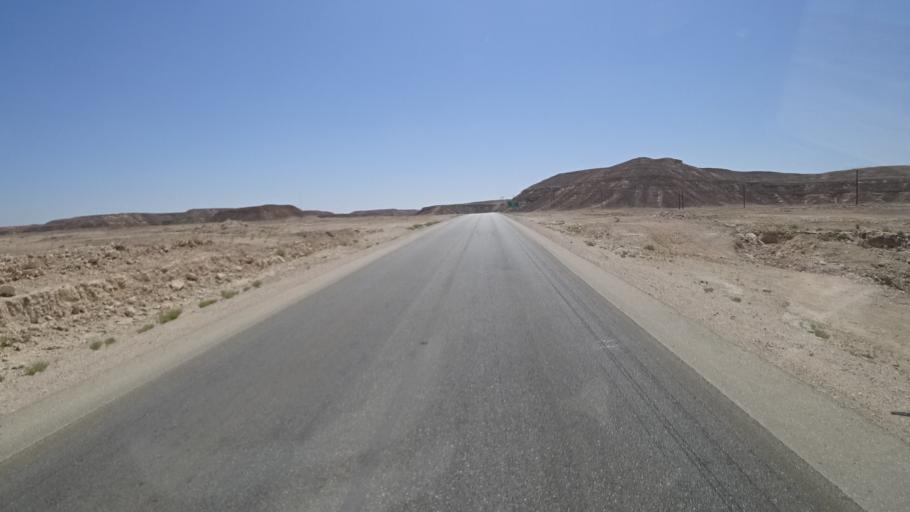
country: OM
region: Zufar
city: Salalah
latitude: 17.5020
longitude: 53.3629
